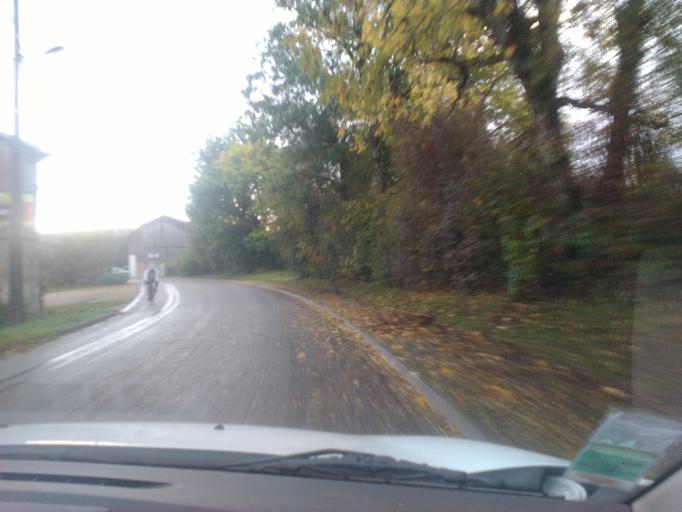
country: FR
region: Lorraine
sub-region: Departement des Vosges
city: Chavelot
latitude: 48.2833
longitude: 6.4676
